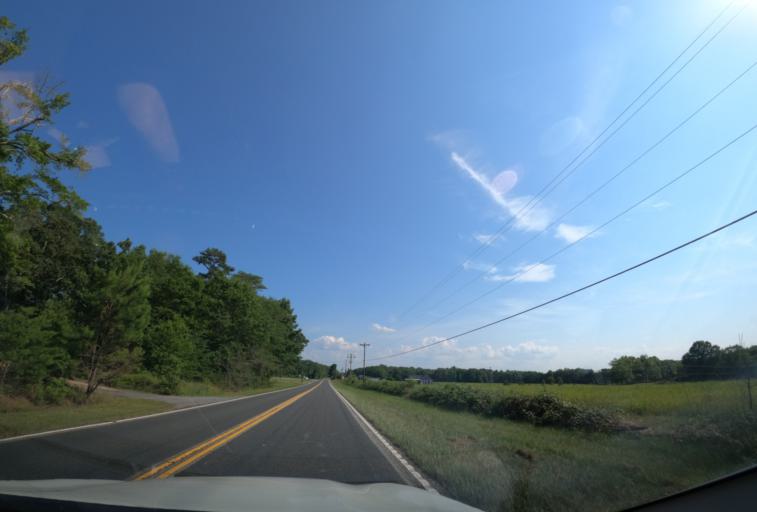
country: US
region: South Carolina
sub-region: Anderson County
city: Belton
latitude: 34.4475
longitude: -82.5498
